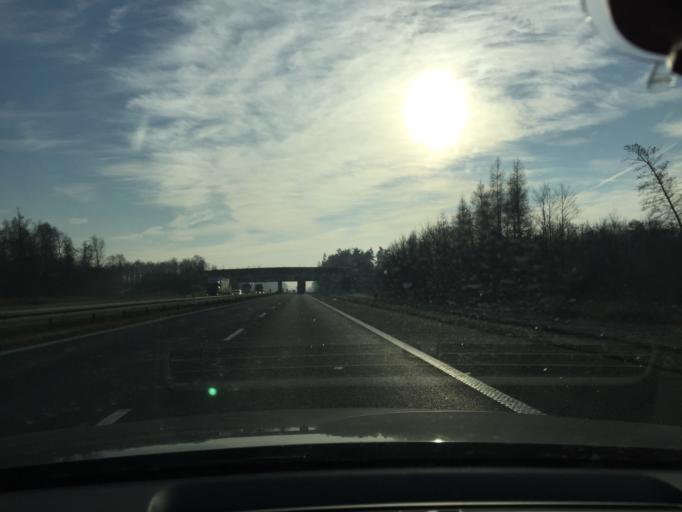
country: PL
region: Silesian Voivodeship
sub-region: Powiat gliwicki
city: Sosnicowice
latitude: 50.3318
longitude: 18.5457
